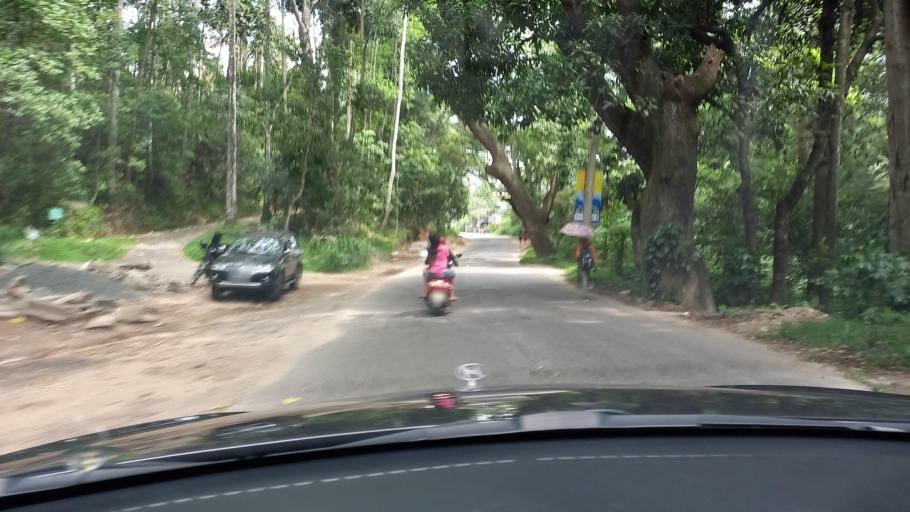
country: LK
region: Central
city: Kandy
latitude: 7.2474
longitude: 80.5983
